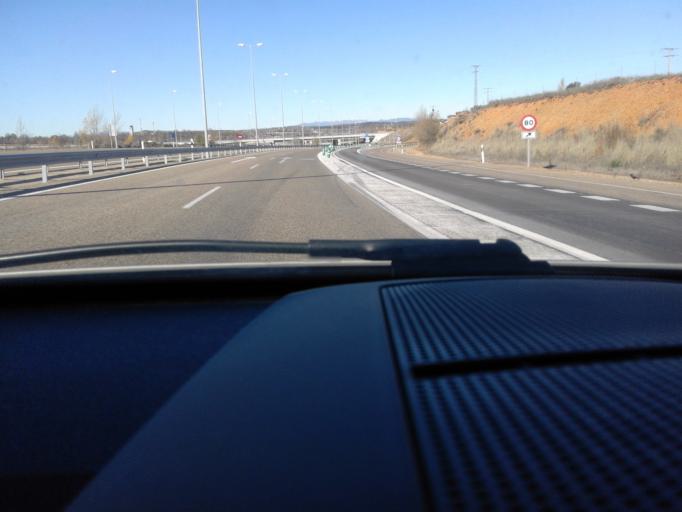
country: ES
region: Castille and Leon
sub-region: Provincia de Leon
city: Valverde de la Virgen
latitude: 42.5641
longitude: -5.6478
